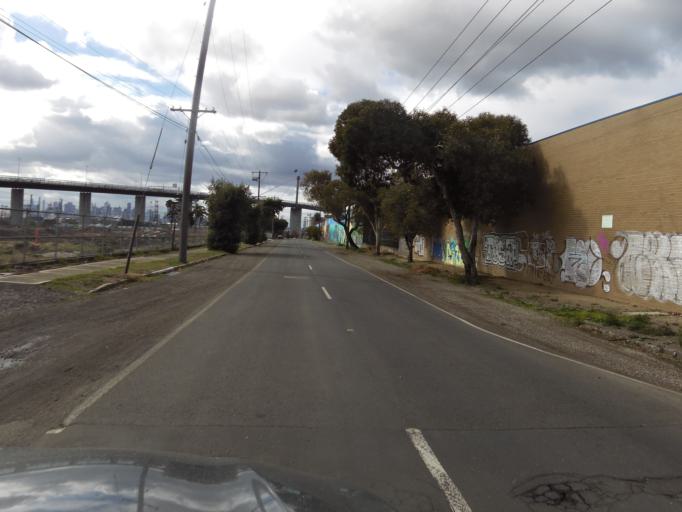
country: AU
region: Victoria
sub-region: Hobsons Bay
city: Spotswood
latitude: -37.8281
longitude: 144.8888
